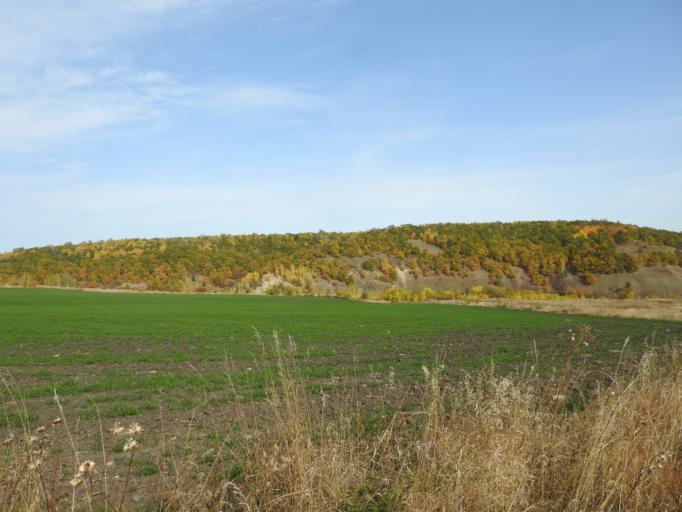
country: RU
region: Saratov
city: Baltay
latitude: 52.5193
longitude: 46.6768
